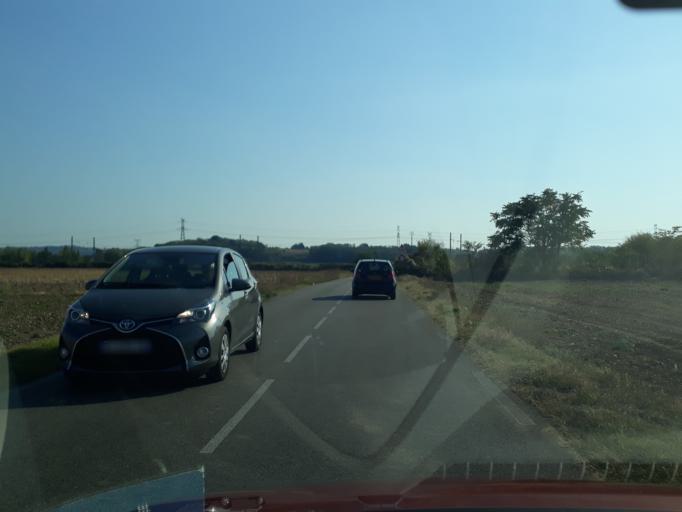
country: FR
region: Rhone-Alpes
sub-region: Departement du Rhone
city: Toussieu
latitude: 45.6756
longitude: 4.9838
